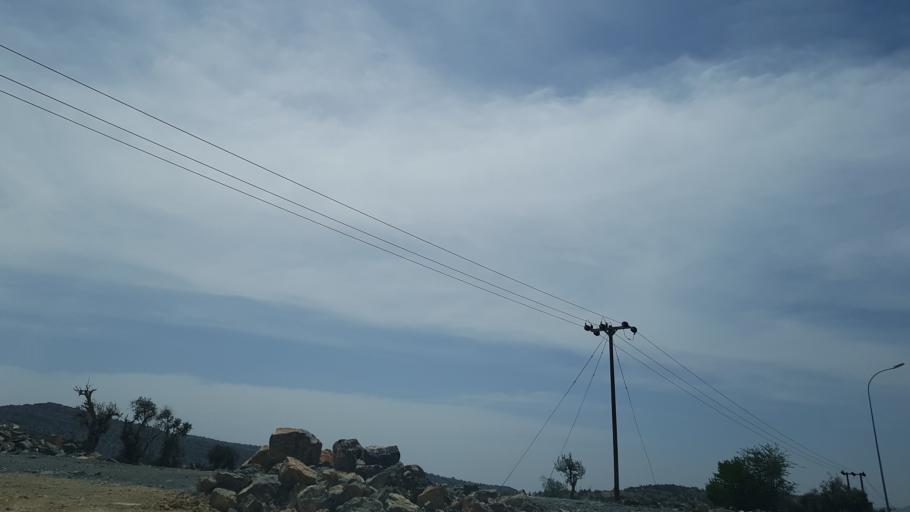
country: OM
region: Al Batinah
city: Bayt al `Awabi
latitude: 23.1378
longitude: 57.5807
